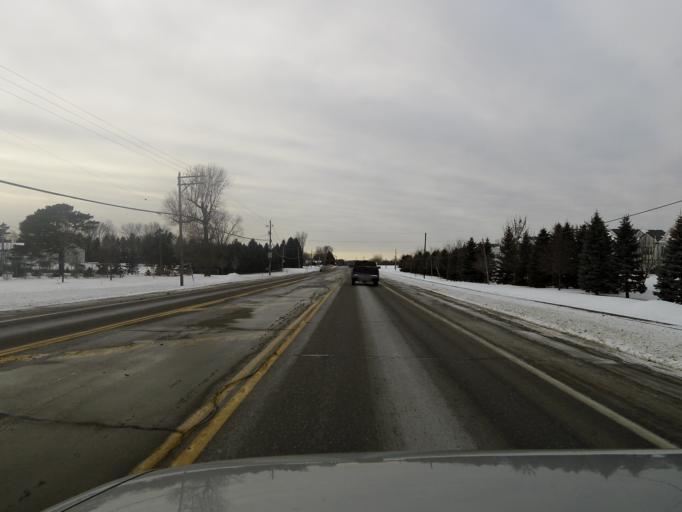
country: US
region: Minnesota
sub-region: Washington County
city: Woodbury
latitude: 44.8909
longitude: -92.9662
